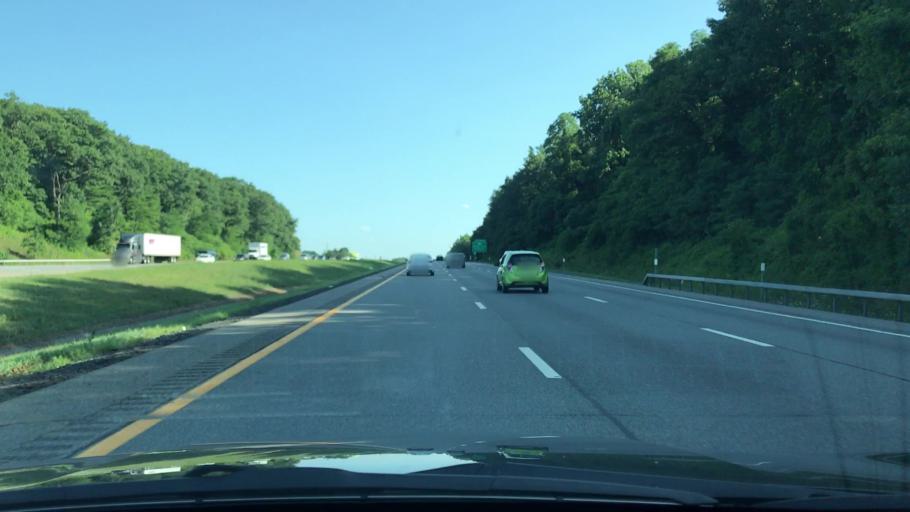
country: US
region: New York
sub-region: Saratoga County
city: Country Knolls
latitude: 42.8832
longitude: -73.7788
